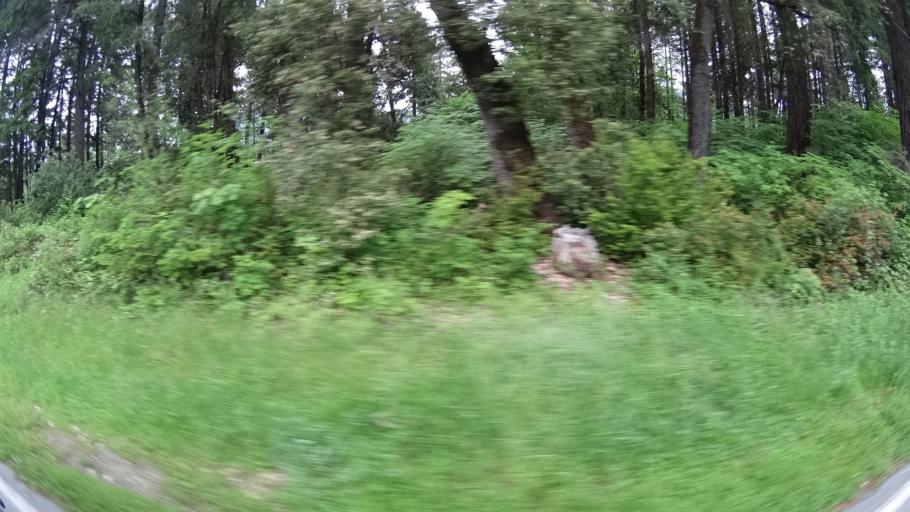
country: US
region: California
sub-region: Humboldt County
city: Willow Creek
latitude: 41.0832
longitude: -123.7037
